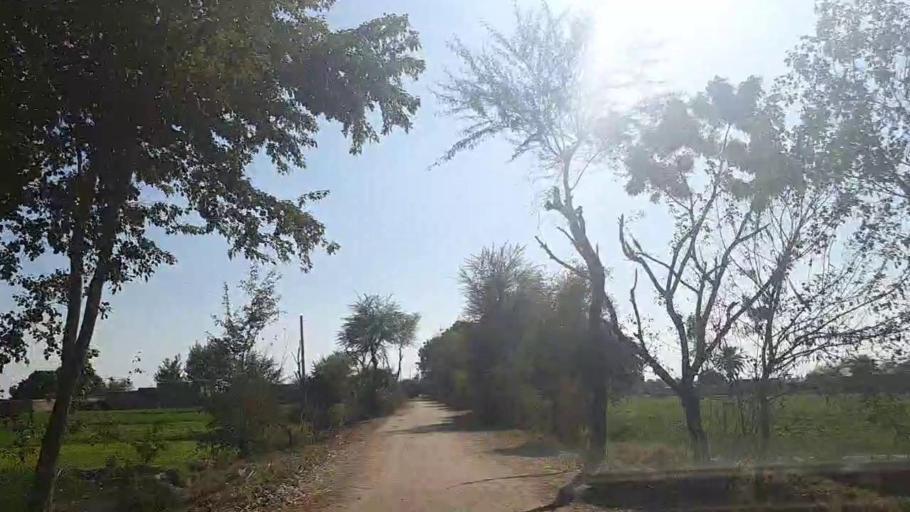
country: PK
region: Sindh
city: Sakrand
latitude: 26.2330
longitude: 68.1998
